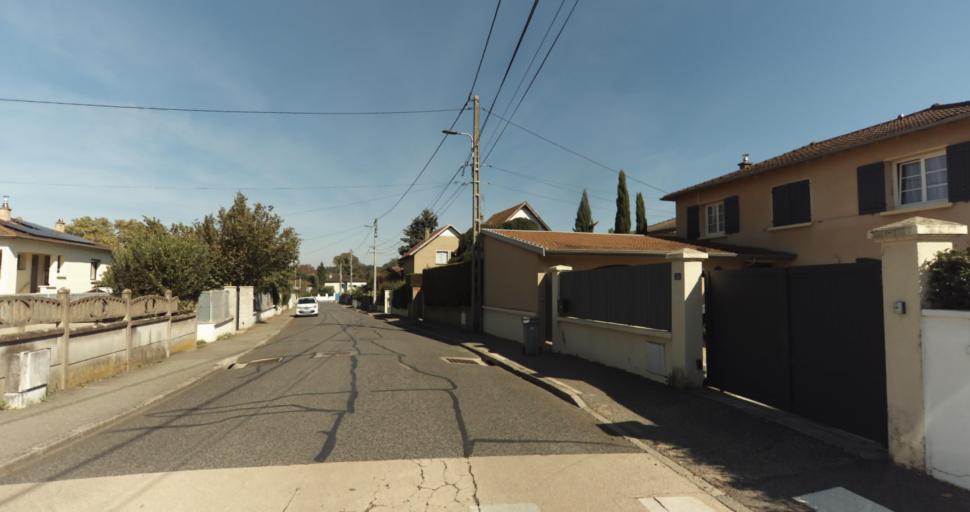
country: FR
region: Rhone-Alpes
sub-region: Departement du Rhone
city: Neuville-sur-Saone
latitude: 45.8724
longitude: 4.8442
